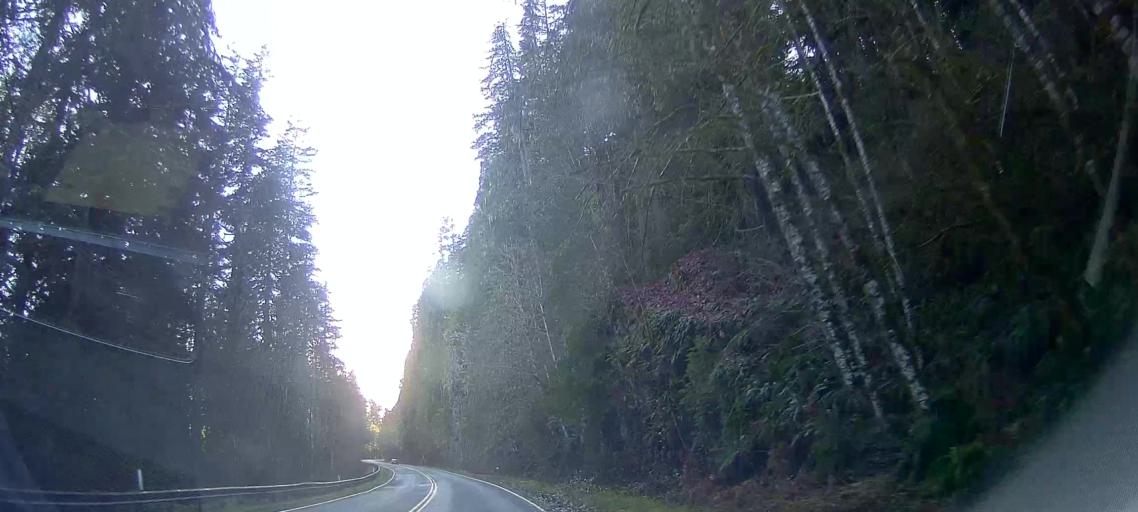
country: US
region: Washington
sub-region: Snohomish County
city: Darrington
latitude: 48.6516
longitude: -121.7114
